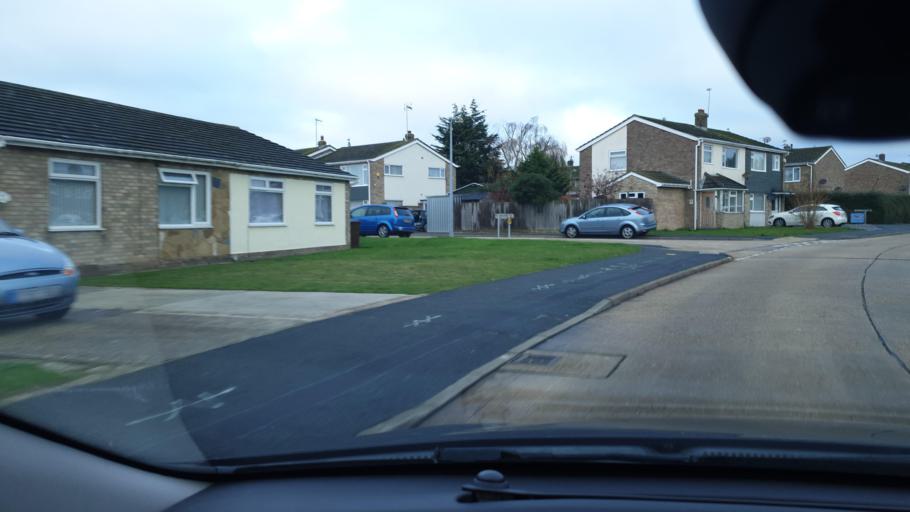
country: GB
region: England
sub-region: Essex
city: Clacton-on-Sea
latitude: 51.7936
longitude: 1.1330
